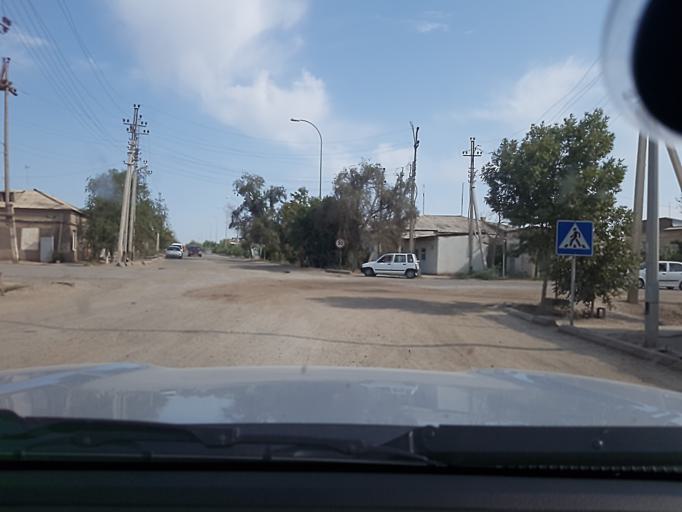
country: TM
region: Dasoguz
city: Dasoguz
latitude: 41.8250
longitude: 59.9806
